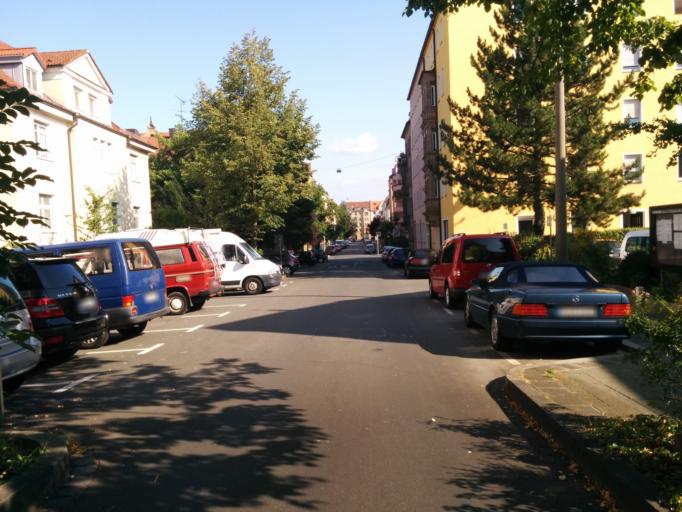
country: DE
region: Bavaria
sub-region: Regierungsbezirk Mittelfranken
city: Nuernberg
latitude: 49.4601
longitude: 11.0787
